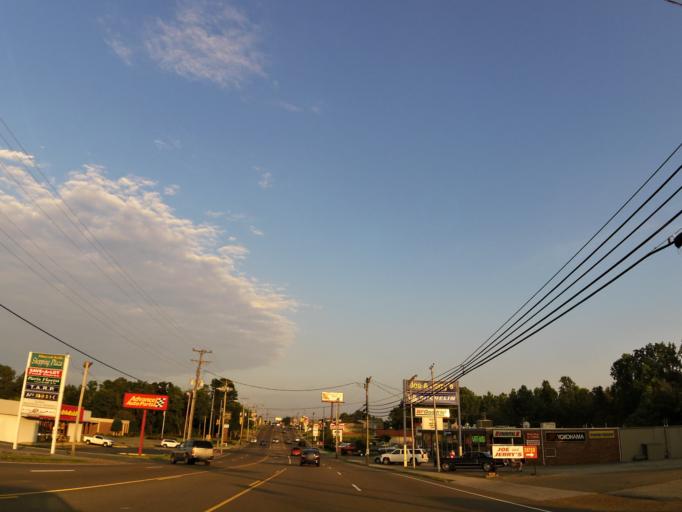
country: US
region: Tennessee
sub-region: Henry County
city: Paris
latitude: 36.2884
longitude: -88.3128
